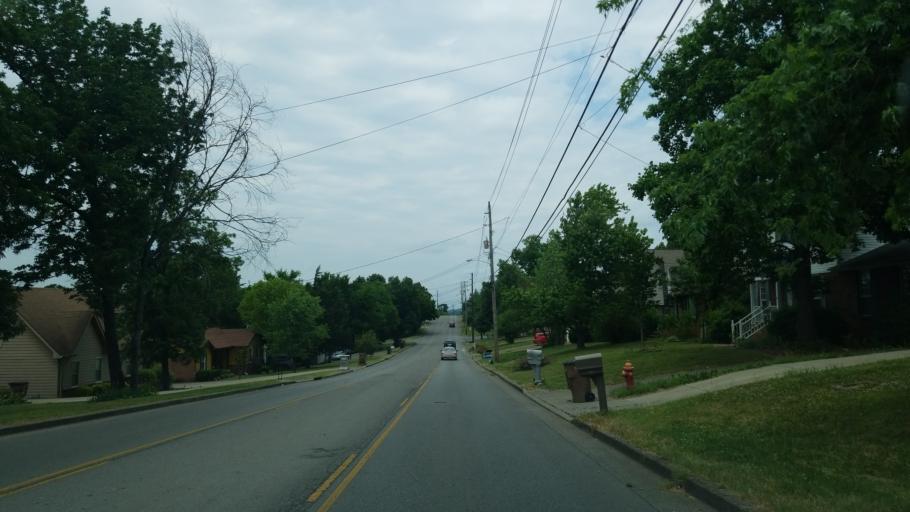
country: US
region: Tennessee
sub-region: Rutherford County
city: La Vergne
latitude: 36.0792
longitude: -86.6070
